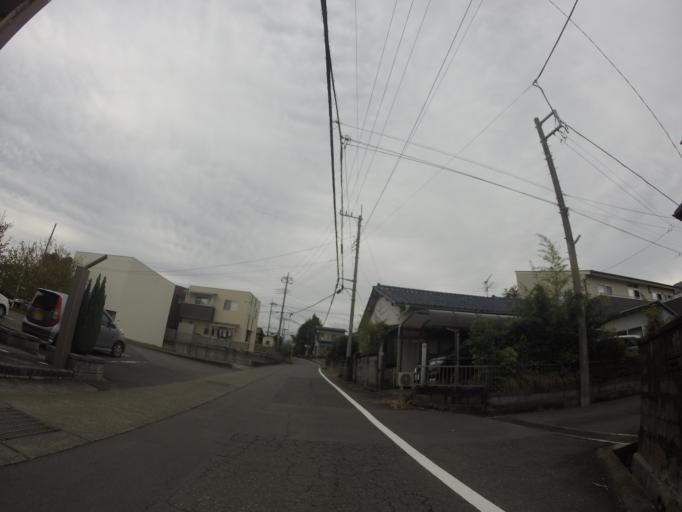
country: JP
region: Shizuoka
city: Fuji
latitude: 35.1957
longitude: 138.6786
